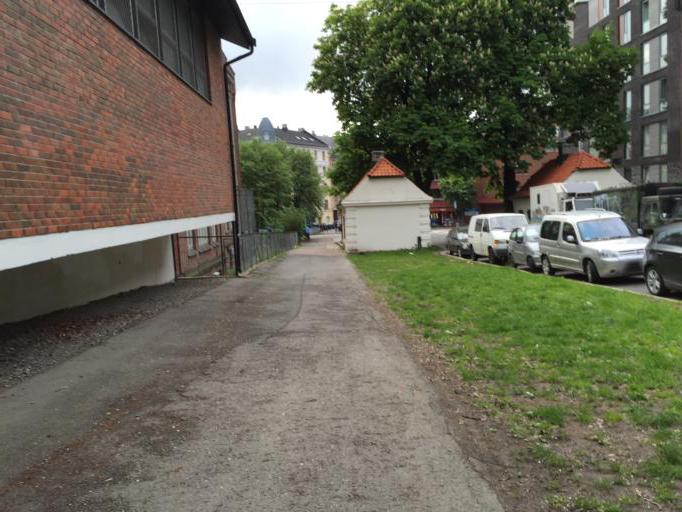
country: NO
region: Oslo
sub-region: Oslo
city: Oslo
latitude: 59.9201
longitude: 10.7692
